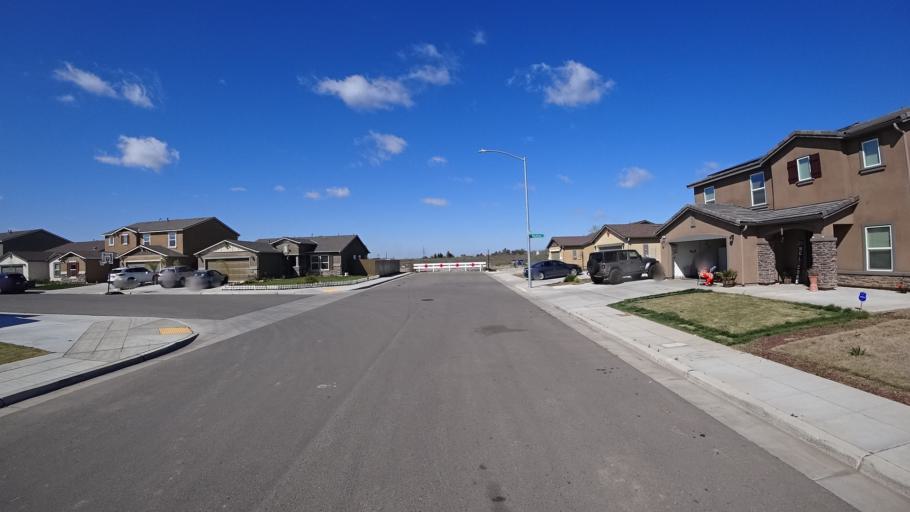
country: US
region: California
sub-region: Fresno County
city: West Park
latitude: 36.7895
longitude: -119.8910
